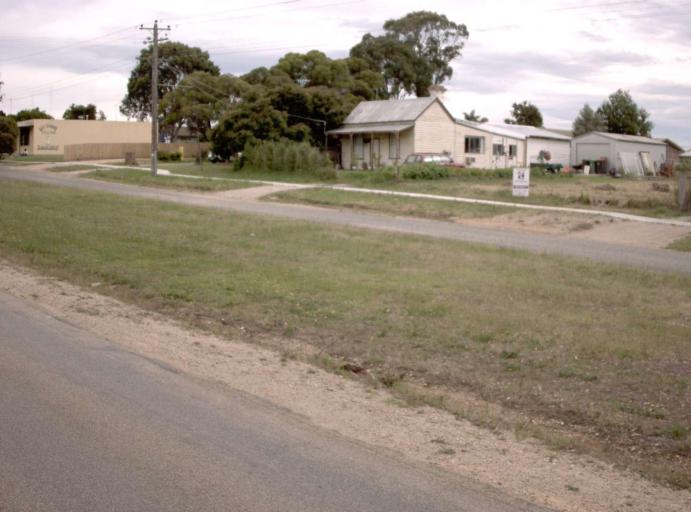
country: AU
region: Victoria
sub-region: East Gippsland
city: Bairnsdale
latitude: -37.8053
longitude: 147.6170
